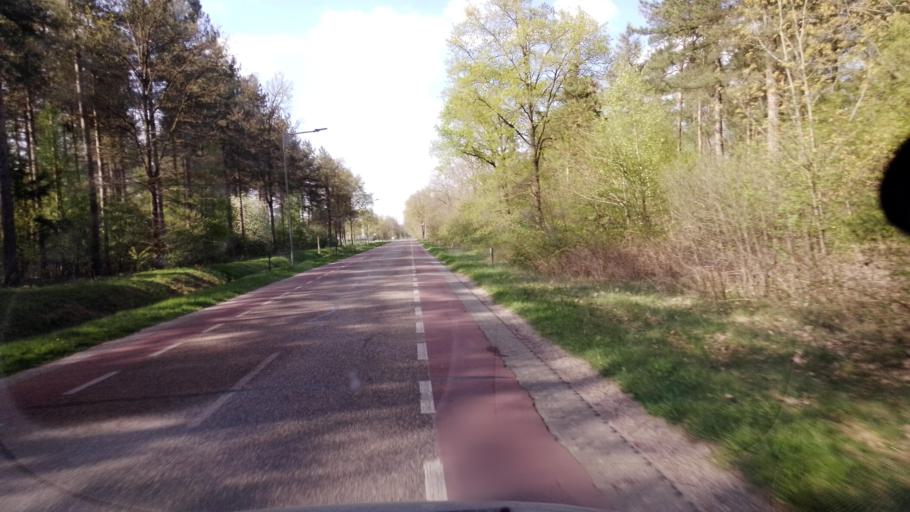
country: NL
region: Limburg
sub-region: Gemeente Venray
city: Venray
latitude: 51.4587
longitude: 5.9708
